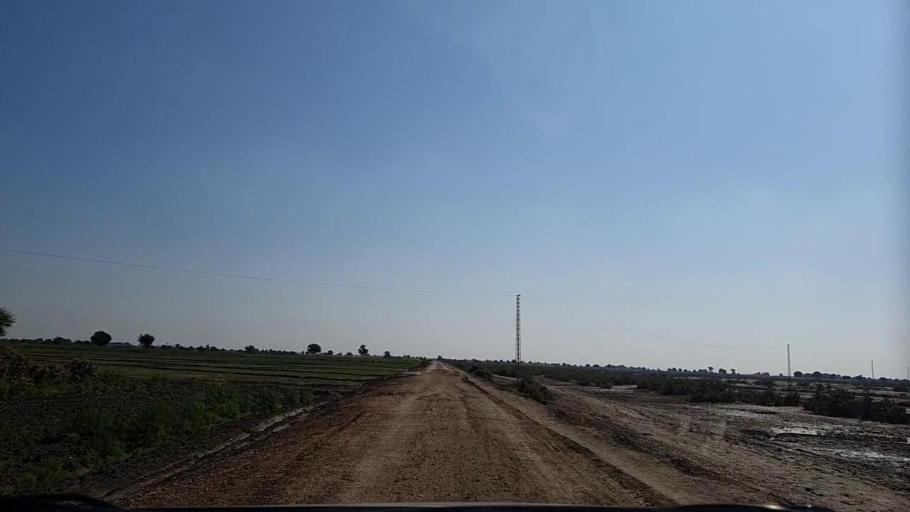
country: PK
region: Sindh
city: Pithoro
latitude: 25.7006
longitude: 69.3405
